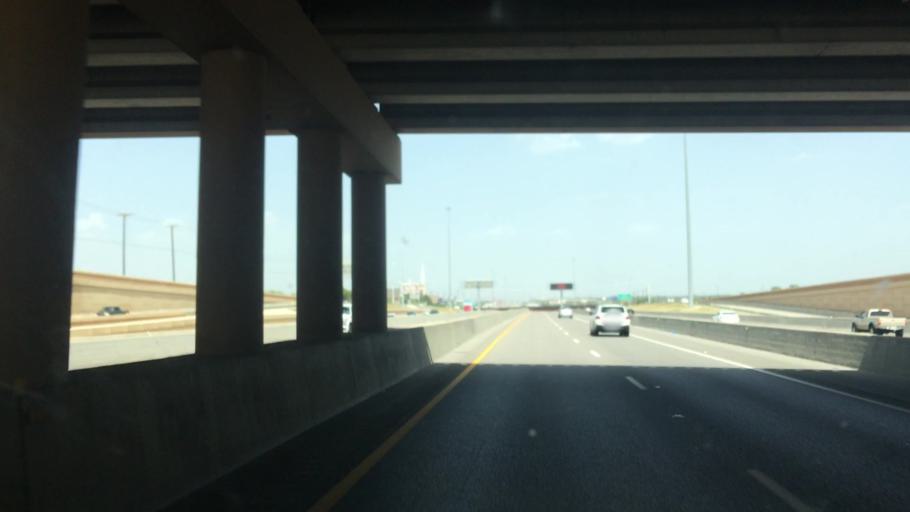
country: US
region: Texas
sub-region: Tarrant County
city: Watauga
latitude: 32.8394
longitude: -97.2767
